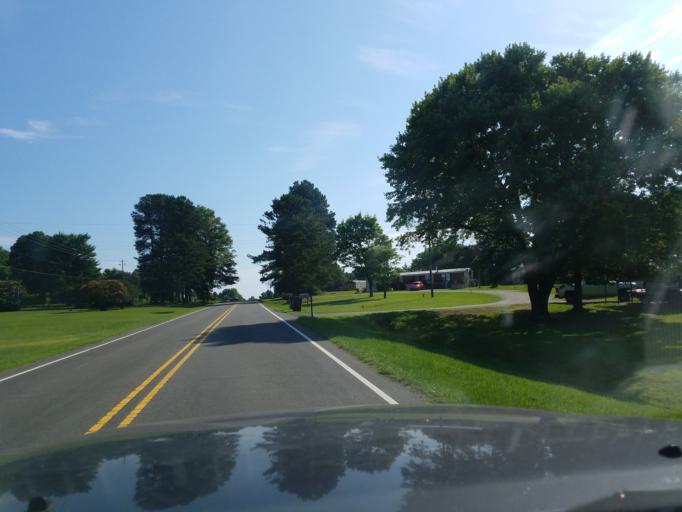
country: US
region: North Carolina
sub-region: Granville County
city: Oxford
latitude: 36.2578
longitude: -78.6577
